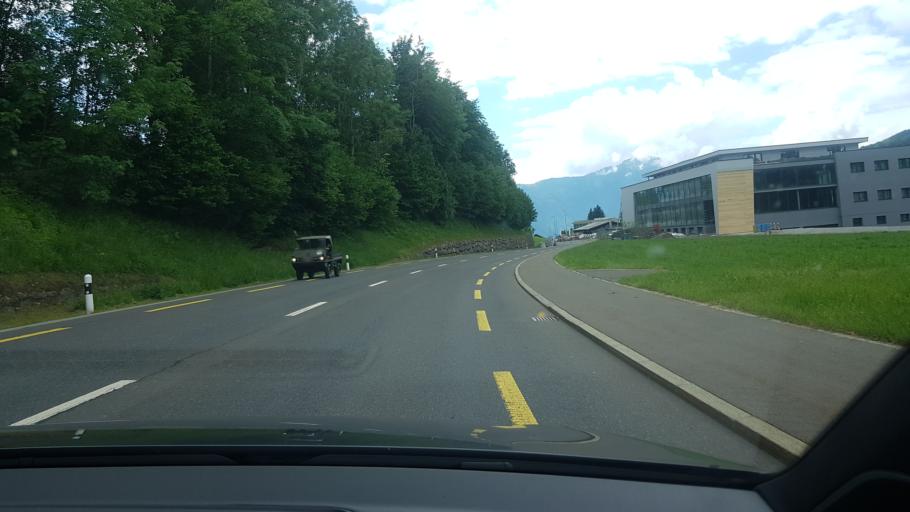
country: CH
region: Schwyz
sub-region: Bezirk Schwyz
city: Sattel
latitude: 47.0752
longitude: 8.6308
